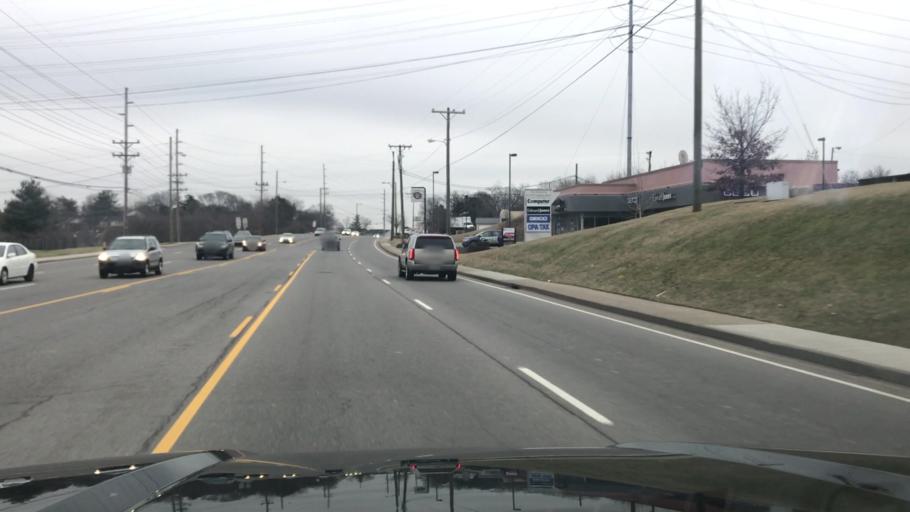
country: US
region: Tennessee
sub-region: Williamson County
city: Brentwood Estates
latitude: 36.0456
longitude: -86.7110
